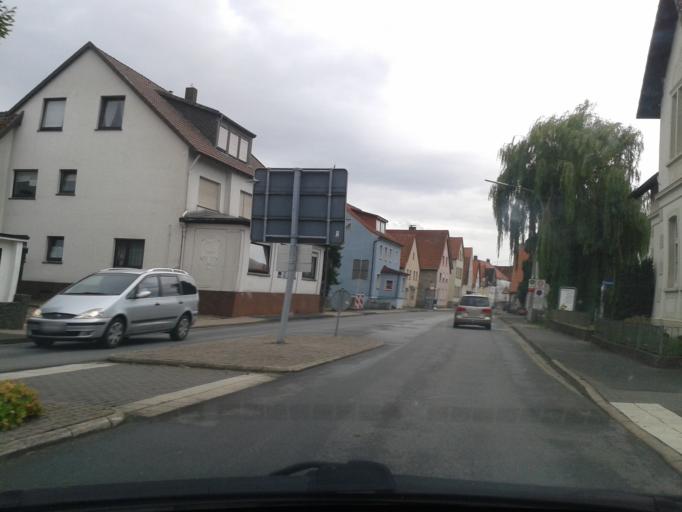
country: DE
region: North Rhine-Westphalia
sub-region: Regierungsbezirk Detmold
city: Horn
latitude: 51.8752
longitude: 8.9433
